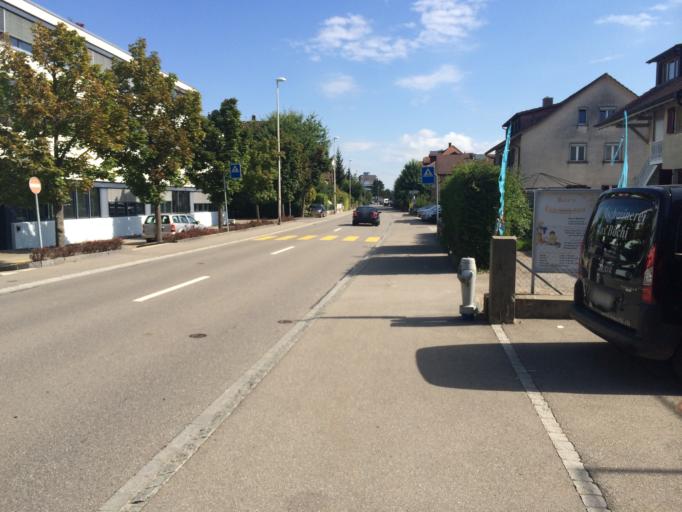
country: CH
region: Bern
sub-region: Bern-Mittelland District
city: Koniz
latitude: 46.9356
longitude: 7.3937
